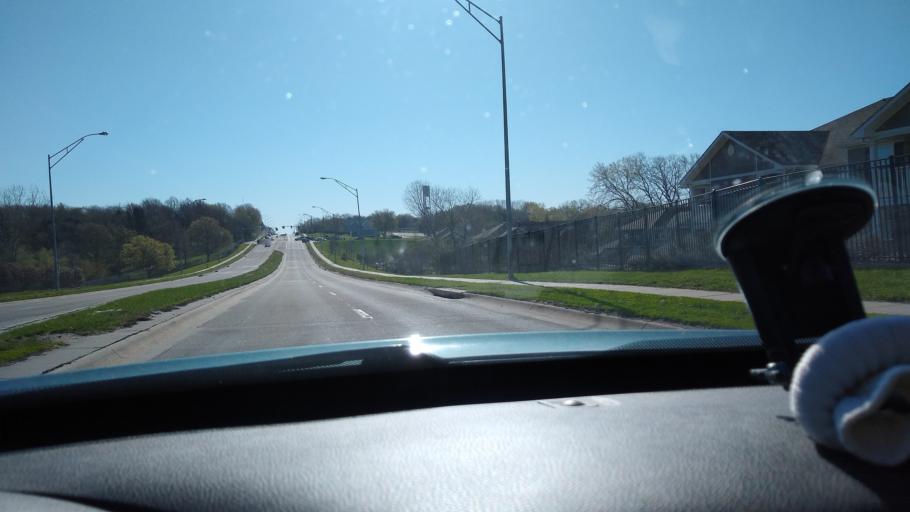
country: US
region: Nebraska
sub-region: Douglas County
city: Ralston
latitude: 41.1908
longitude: -96.0659
